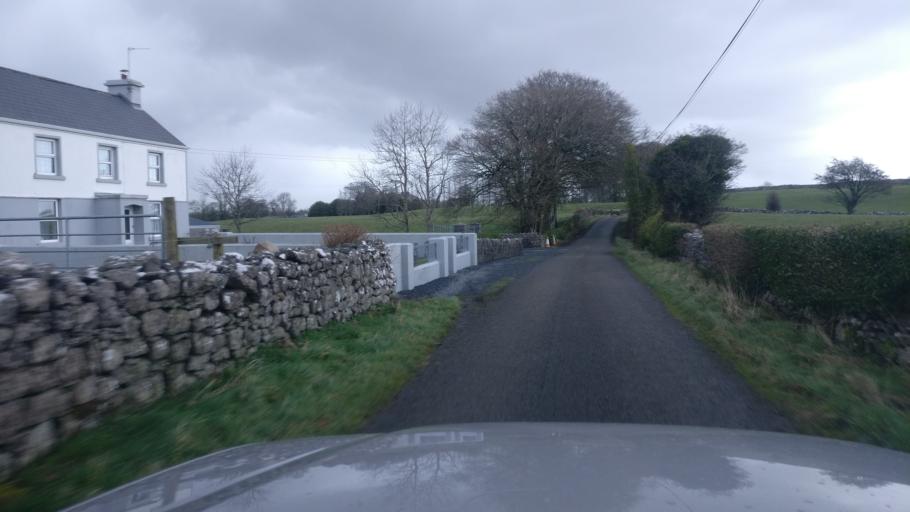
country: IE
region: Connaught
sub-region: County Galway
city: Loughrea
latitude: 53.1831
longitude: -8.6747
